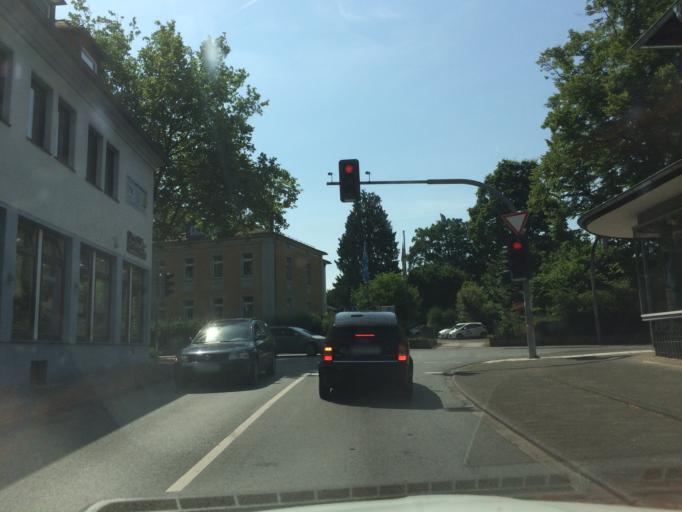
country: DE
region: Hesse
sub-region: Regierungsbezirk Kassel
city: Hofgeismar
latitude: 51.4945
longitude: 9.3859
